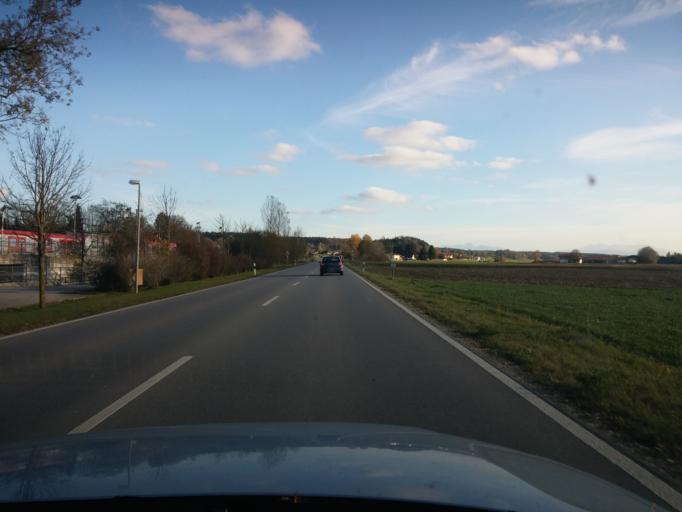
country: DE
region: Bavaria
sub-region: Upper Bavaria
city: Aying
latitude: 47.9690
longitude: 11.7688
